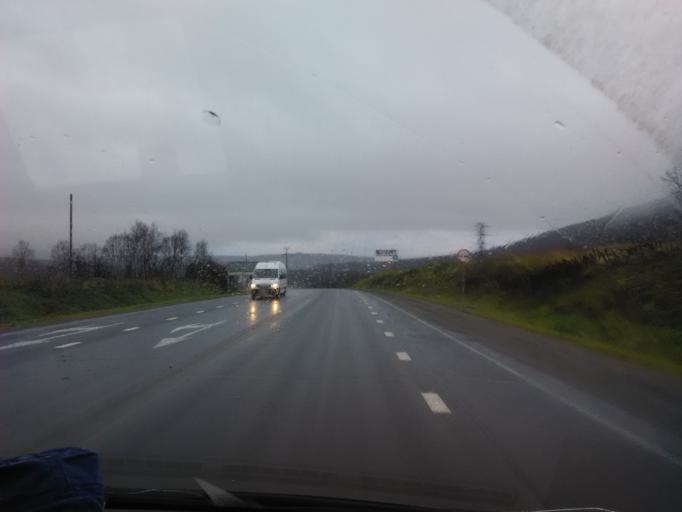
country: RU
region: Murmansk
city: Molochnyy
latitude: 68.8486
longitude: 33.0876
